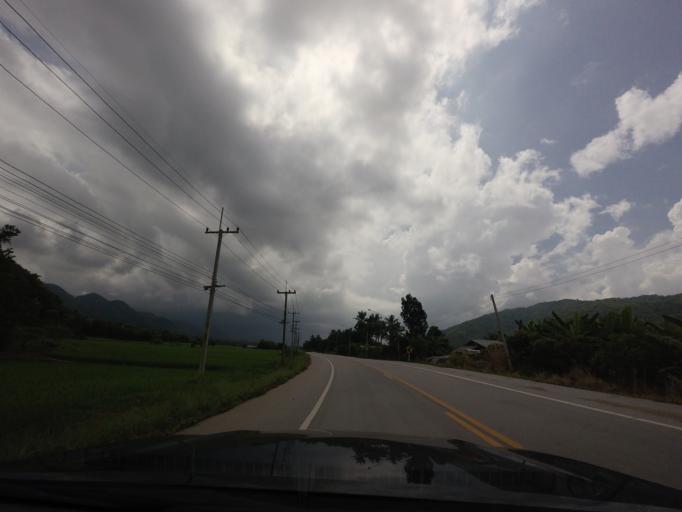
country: TH
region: Loei
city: Pak Chom
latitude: 18.0191
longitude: 101.7617
